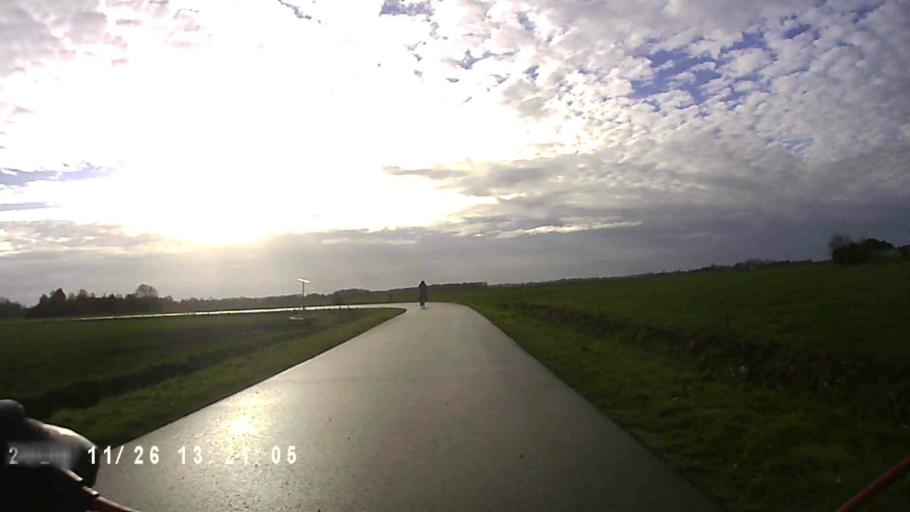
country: NL
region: Groningen
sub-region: Gemeente Delfzijl
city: Delfzijl
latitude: 53.3492
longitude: 6.8914
